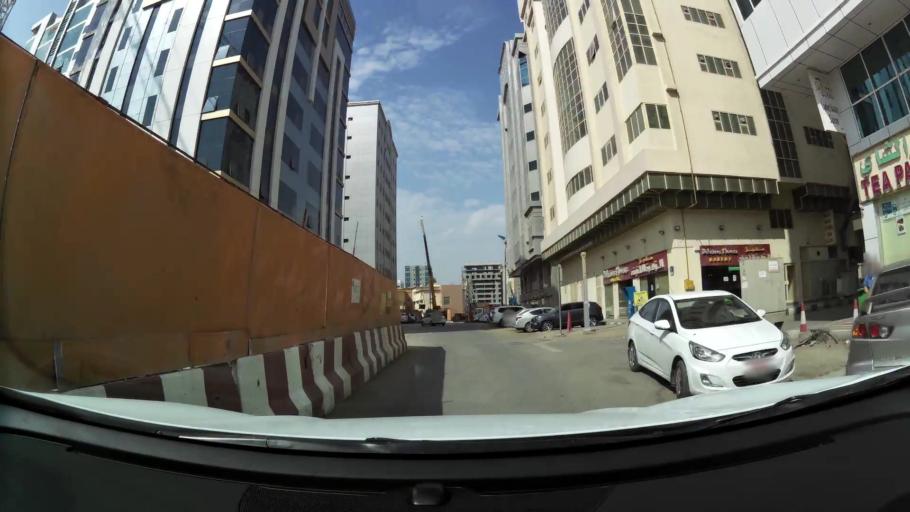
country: AE
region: Abu Dhabi
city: Abu Dhabi
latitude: 24.3405
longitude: 54.5337
